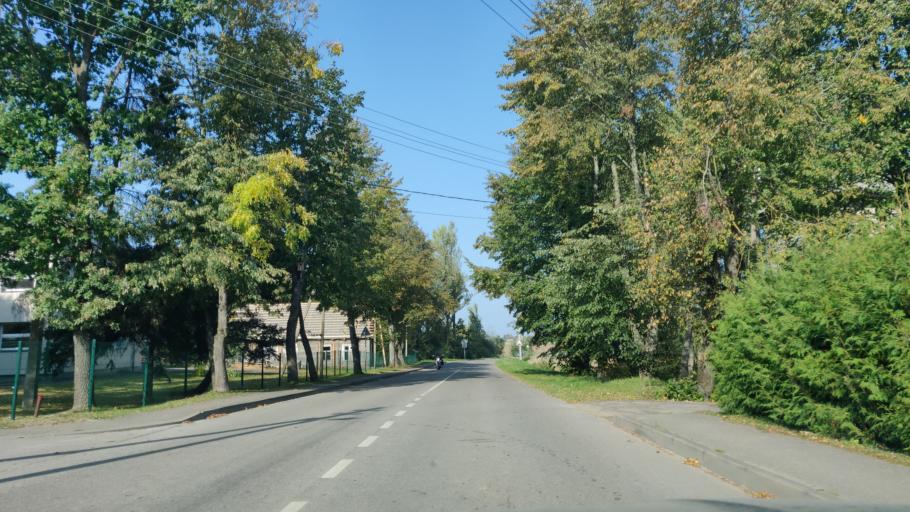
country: LT
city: Sirvintos
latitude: 54.9511
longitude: 24.8388
